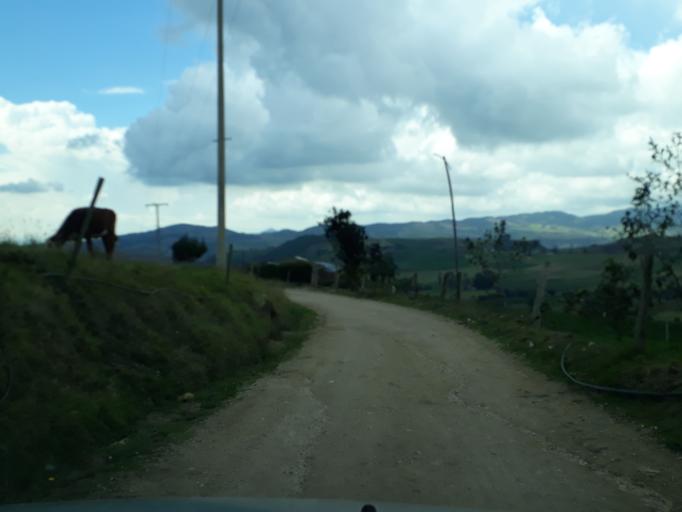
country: CO
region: Cundinamarca
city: Lenguazaque
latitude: 5.2430
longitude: -73.6759
